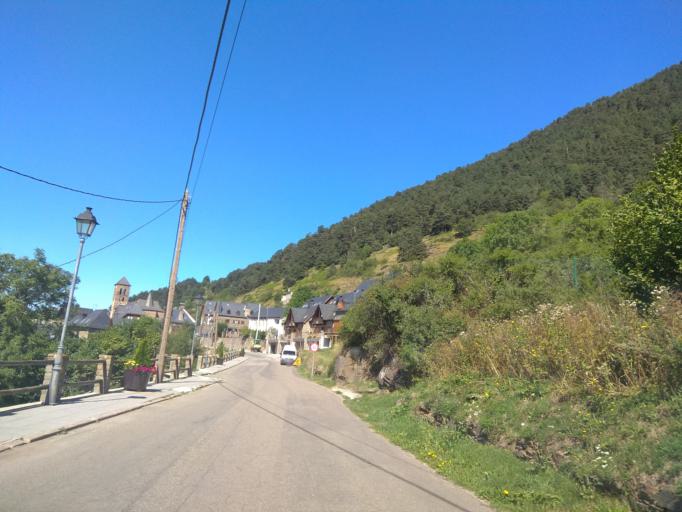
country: ES
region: Catalonia
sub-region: Provincia de Lleida
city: Les
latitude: 42.7467
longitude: 0.7291
